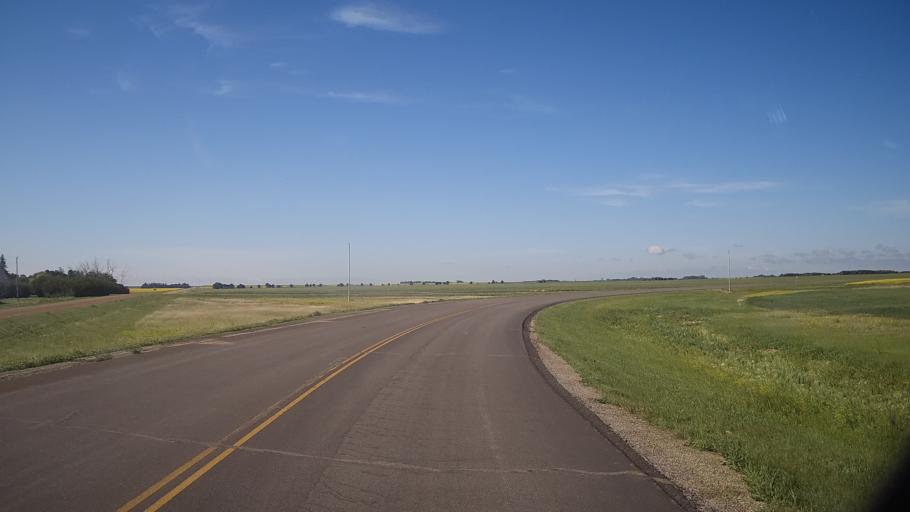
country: CA
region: Saskatchewan
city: Watrous
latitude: 51.6804
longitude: -105.3811
